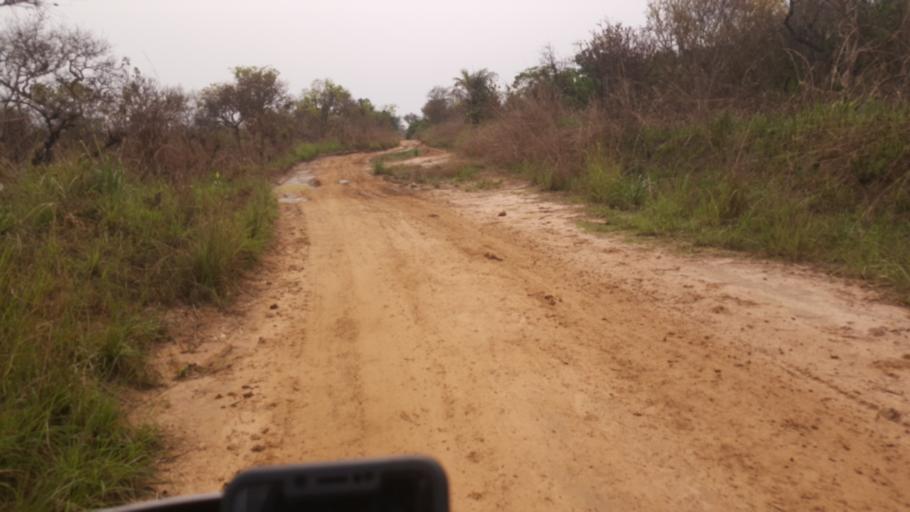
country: CD
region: Bandundu
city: Bandundu
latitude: -3.4543
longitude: 17.7473
